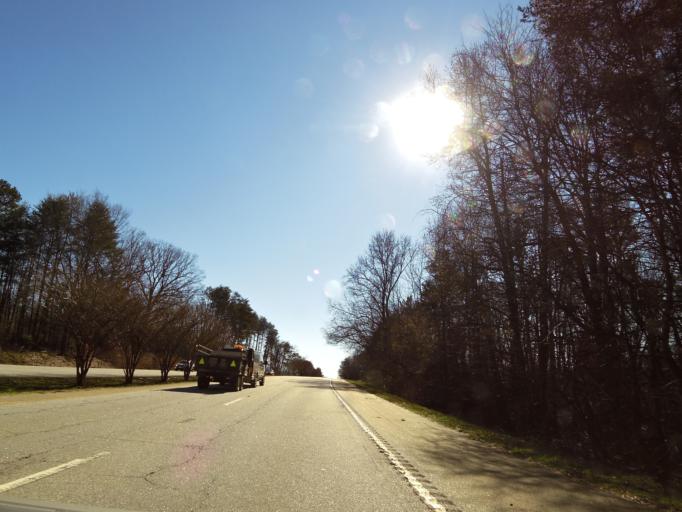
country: US
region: South Carolina
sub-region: Greenville County
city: Travelers Rest
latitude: 34.9326
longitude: -82.4332
